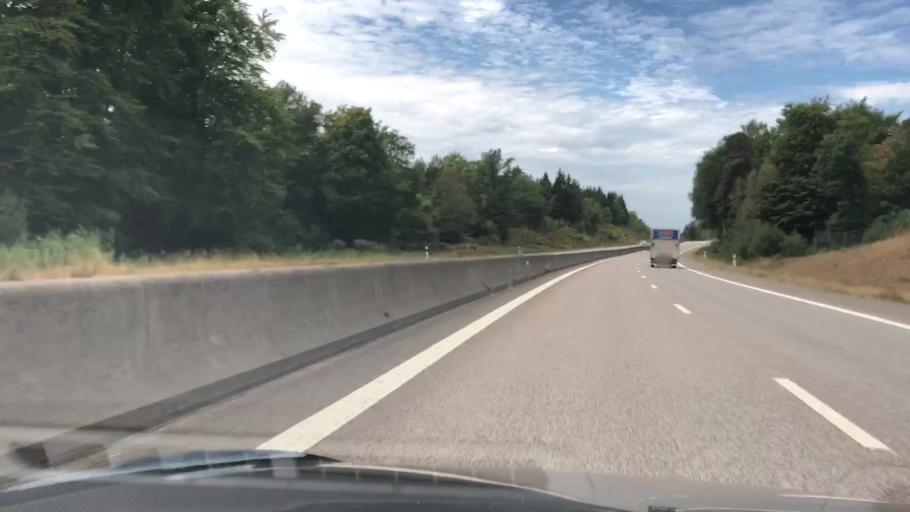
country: SE
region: Blekinge
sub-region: Karlskrona Kommun
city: Nattraby
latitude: 56.2099
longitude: 15.5603
